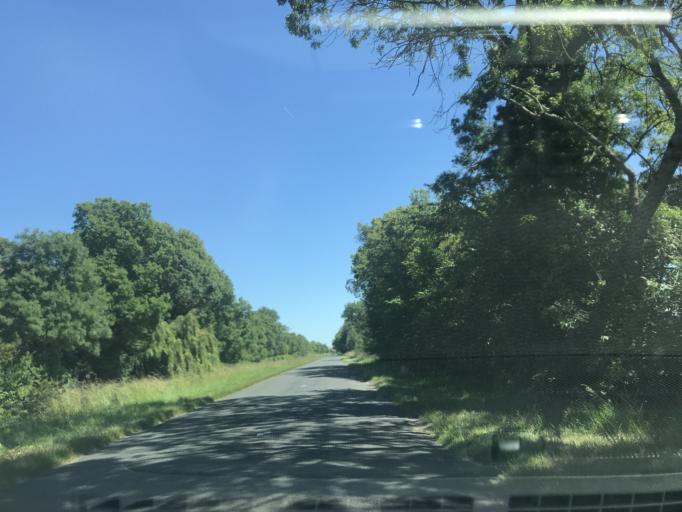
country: FR
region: Poitou-Charentes
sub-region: Departement de la Charente-Maritime
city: Mortagne-sur-Gironde
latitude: 45.4752
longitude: -0.7889
